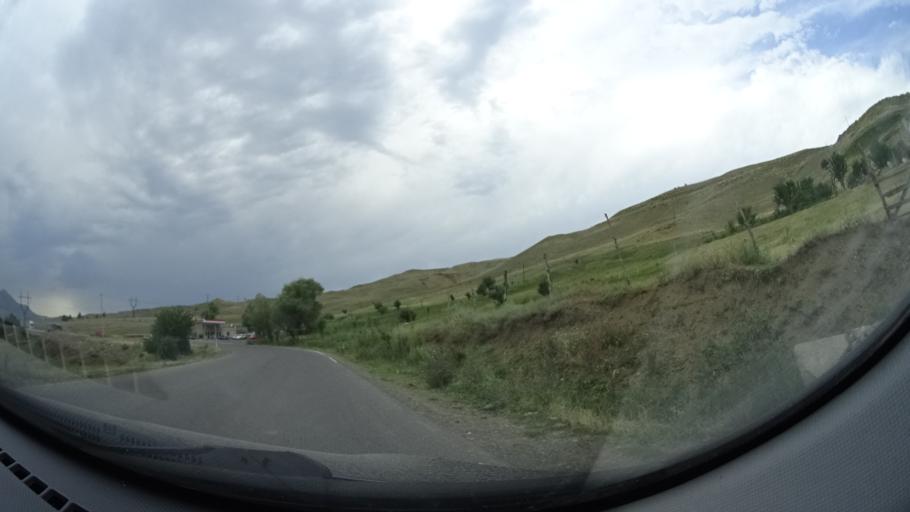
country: GE
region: Samtskhe-Javakheti
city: Aspindza
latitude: 41.5958
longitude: 43.2252
